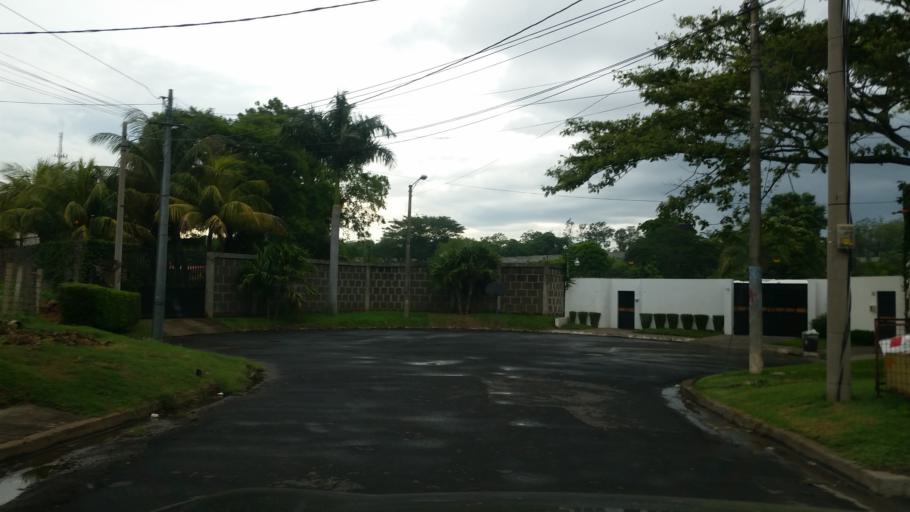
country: NI
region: Managua
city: Managua
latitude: 12.0804
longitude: -86.2480
